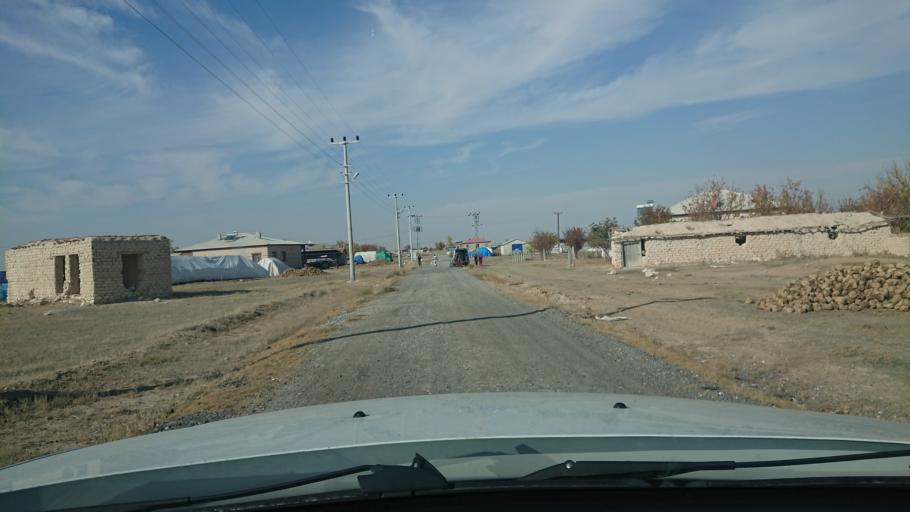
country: TR
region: Aksaray
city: Sultanhani
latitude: 38.2546
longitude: 33.4802
